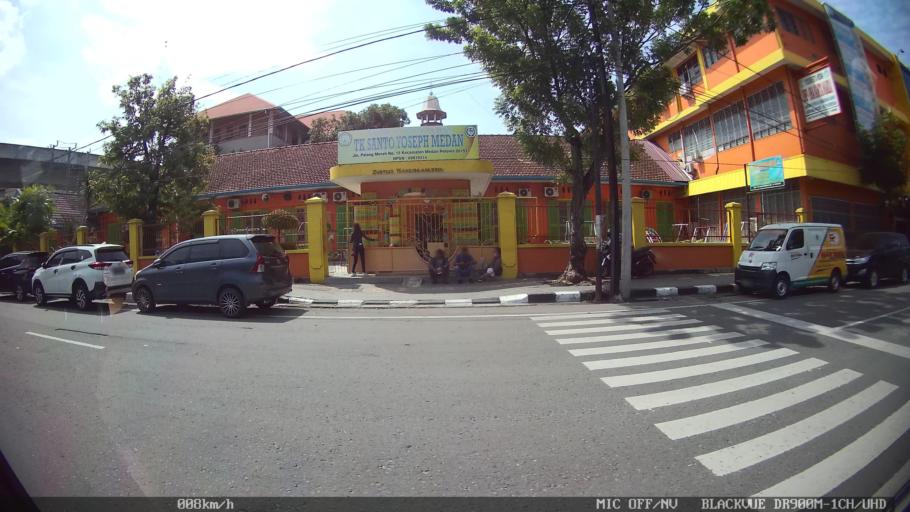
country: ID
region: North Sumatra
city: Medan
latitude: 3.5848
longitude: 98.6818
